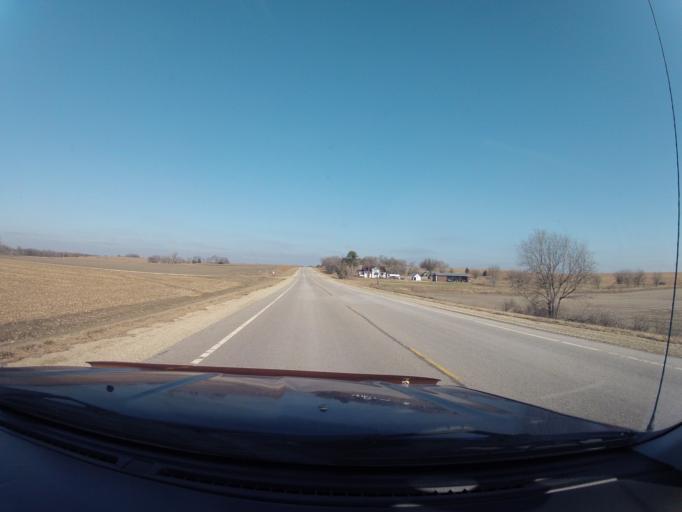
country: US
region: Kansas
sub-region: Marshall County
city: Blue Rapids
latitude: 39.5796
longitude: -96.7502
